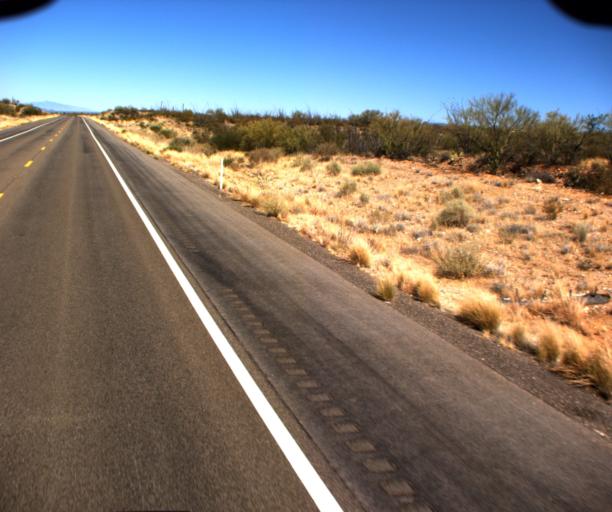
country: US
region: Arizona
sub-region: Pima County
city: Three Points
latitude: 32.0374
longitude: -111.5155
